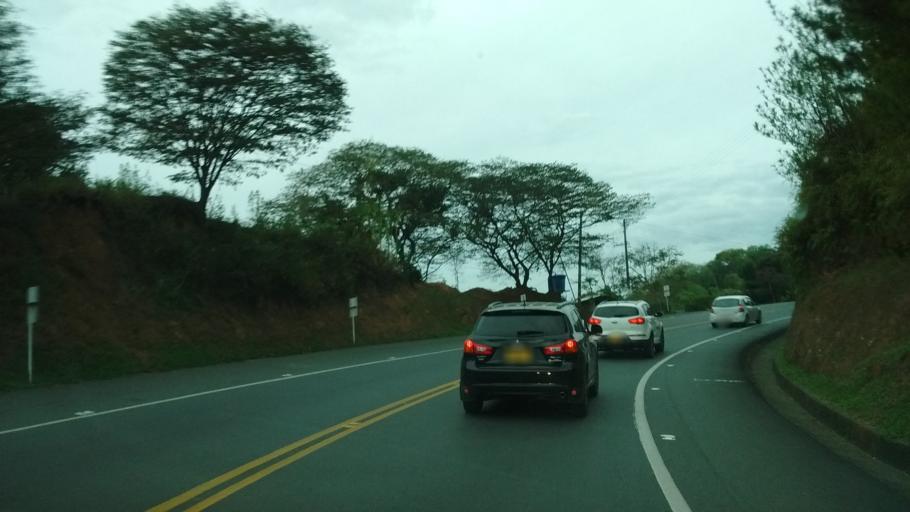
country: CO
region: Cauca
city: Caldono
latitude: 2.7964
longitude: -76.5532
